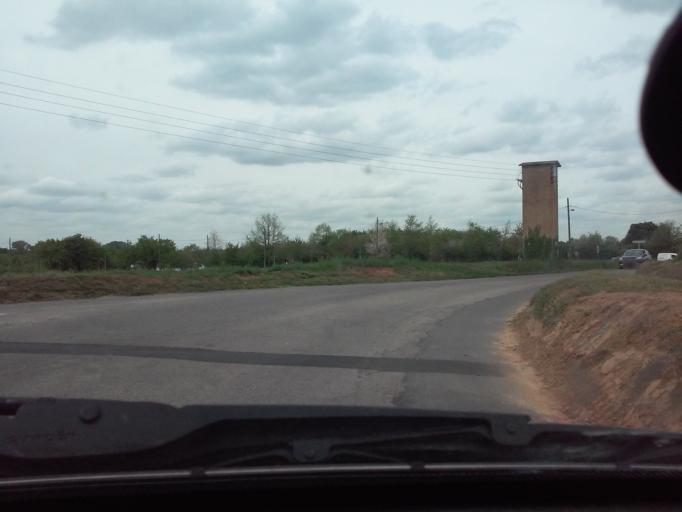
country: FR
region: Brittany
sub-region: Departement d'Ille-et-Vilaine
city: Saint-Jacques-de-la-Lande
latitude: 48.0907
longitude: -1.7389
